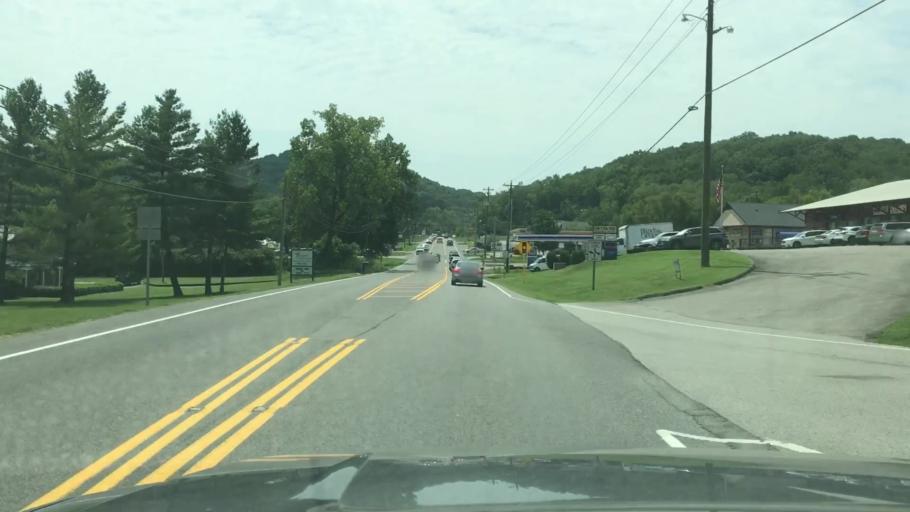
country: US
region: Tennessee
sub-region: Williamson County
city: Franklin
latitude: 35.9991
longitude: -86.8859
